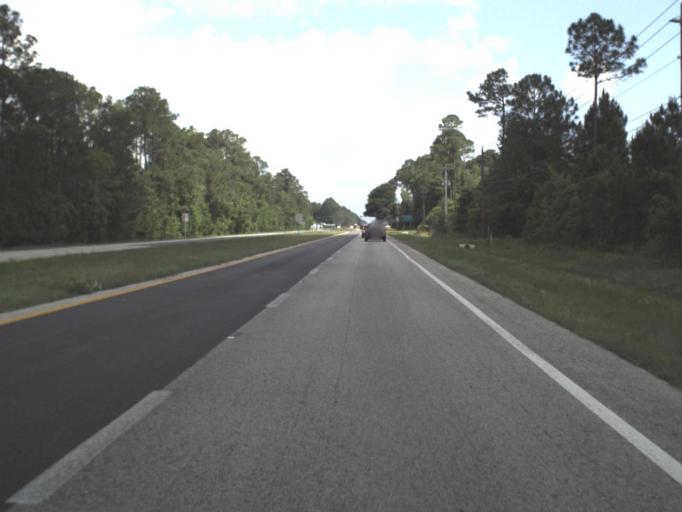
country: US
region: Florida
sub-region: Saint Johns County
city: Saint Augustine Shores
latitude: 29.7515
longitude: -81.3119
